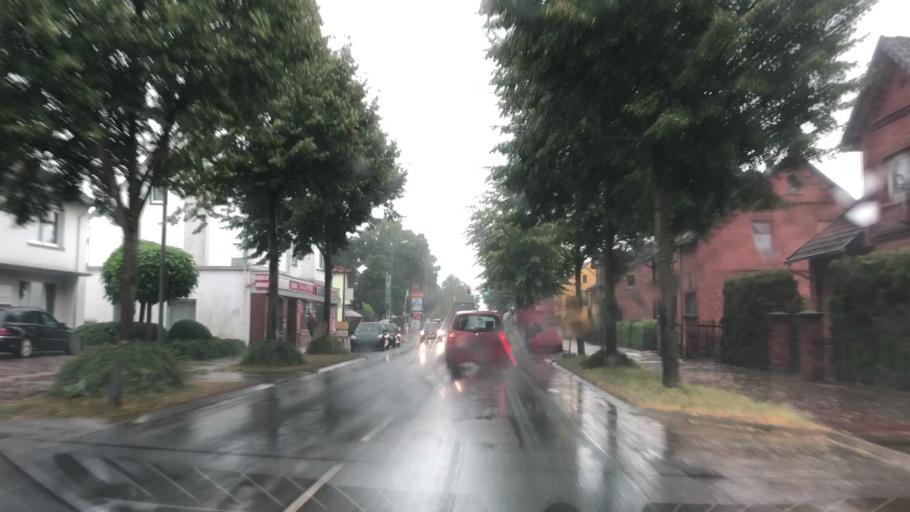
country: DE
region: North Rhine-Westphalia
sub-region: Regierungsbezirk Detmold
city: Minden
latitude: 52.2853
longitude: 8.9480
